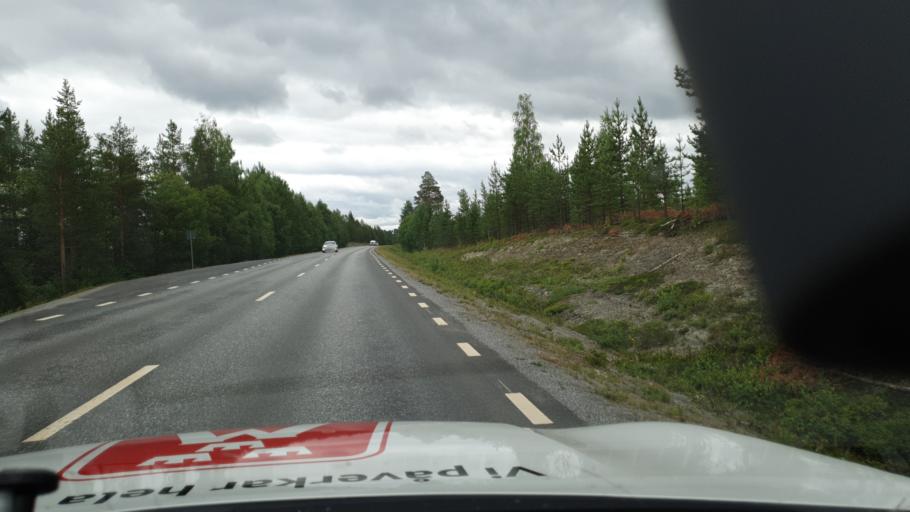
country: SE
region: Vaesterbotten
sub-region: Lycksele Kommun
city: Soderfors
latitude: 64.8711
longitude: 17.9166
